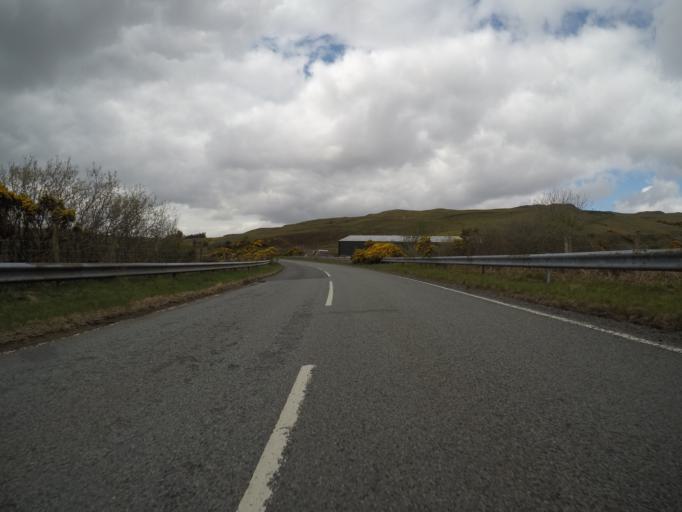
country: GB
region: Scotland
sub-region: Highland
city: Isle of Skye
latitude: 57.3285
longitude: -6.3339
